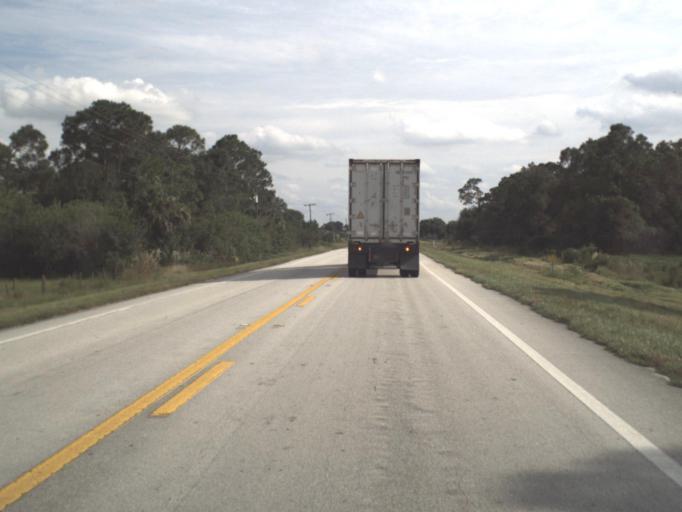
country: US
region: Florida
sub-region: Okeechobee County
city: Taylor Creek
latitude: 27.2204
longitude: -80.7645
